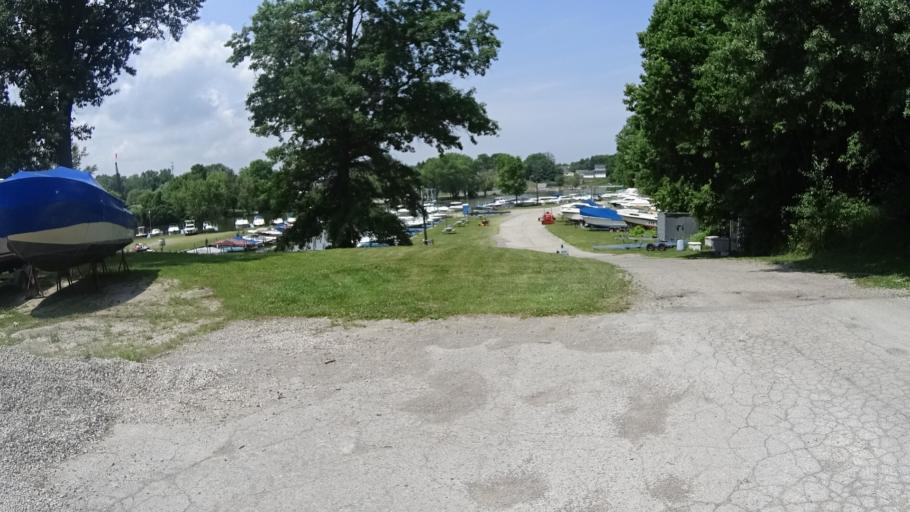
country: US
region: Ohio
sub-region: Lorain County
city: Vermilion
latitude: 41.4207
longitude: -82.3526
